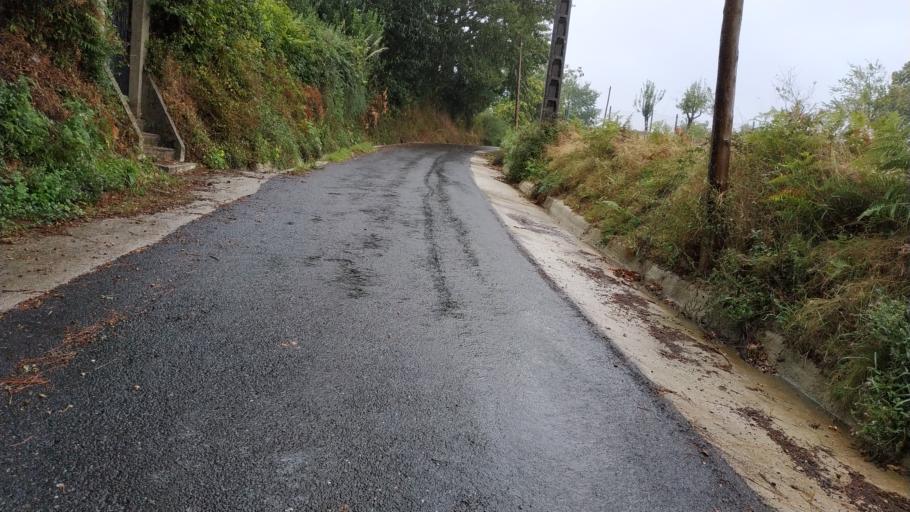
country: ES
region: Galicia
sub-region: Provincia da Coruna
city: Negreira
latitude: 42.9084
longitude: -8.7424
